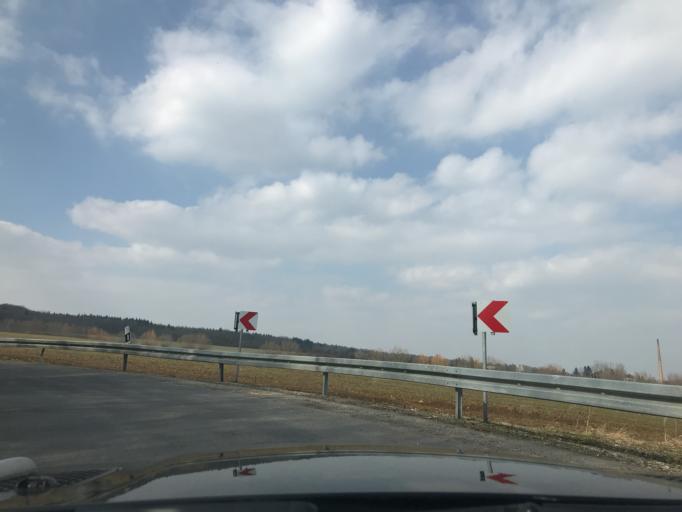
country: DE
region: Thuringia
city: Oberdorla
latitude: 51.1854
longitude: 10.4026
